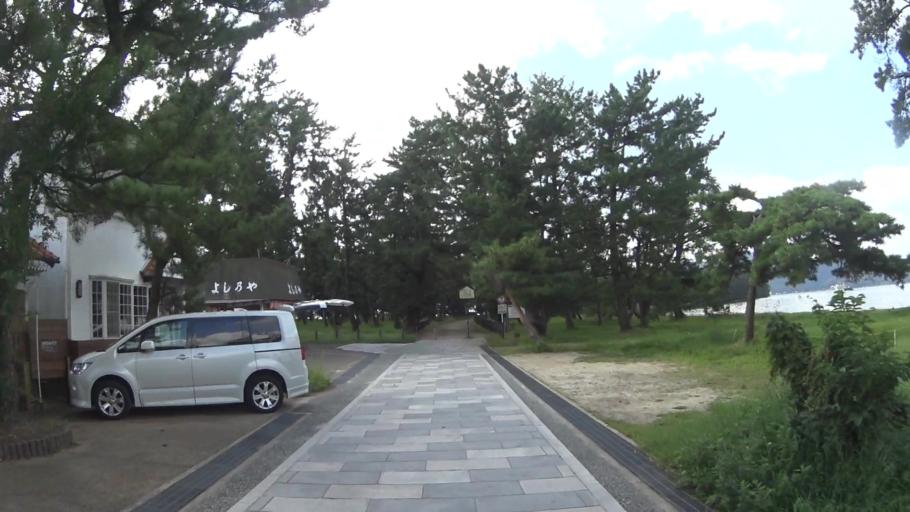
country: JP
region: Kyoto
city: Miyazu
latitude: 35.5784
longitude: 135.1980
